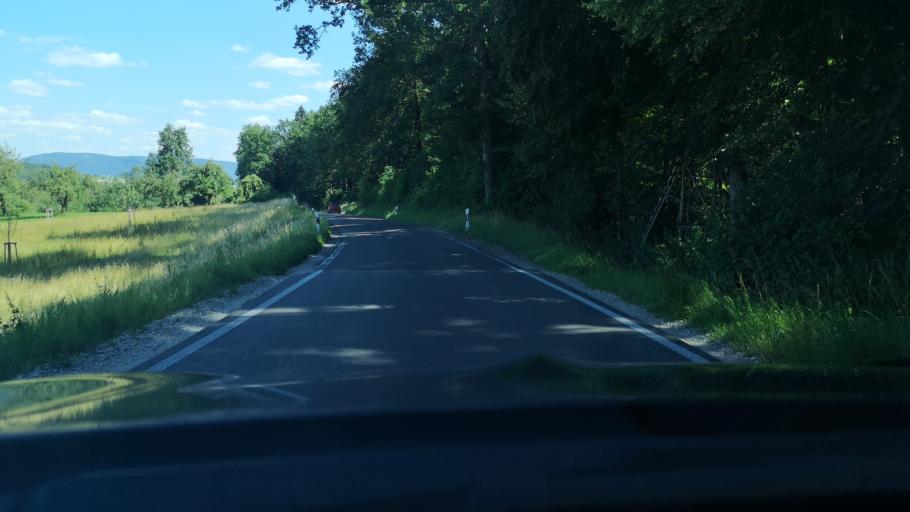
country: DE
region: Baden-Wuerttemberg
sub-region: Regierungsbezirk Stuttgart
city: Altenriet
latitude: 48.5842
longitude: 9.2185
